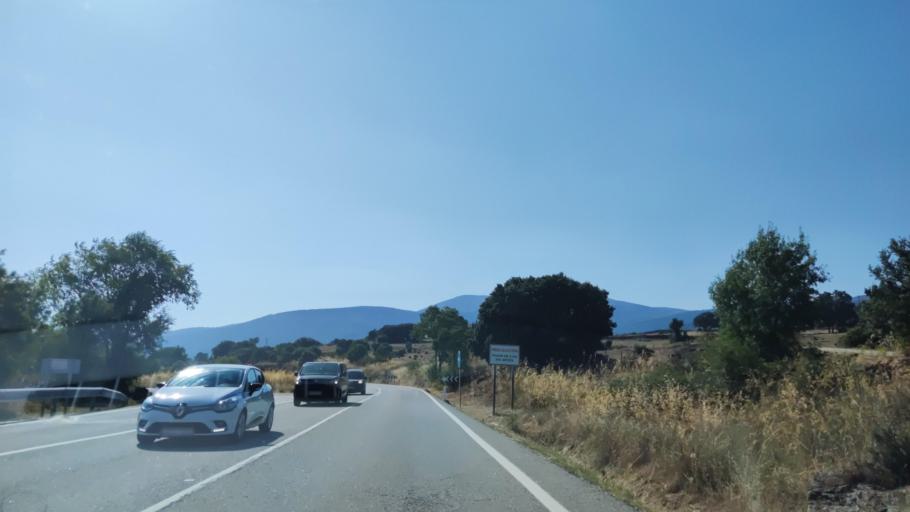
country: ES
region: Madrid
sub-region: Provincia de Madrid
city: Lozoya
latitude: 40.9478
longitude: -3.7634
